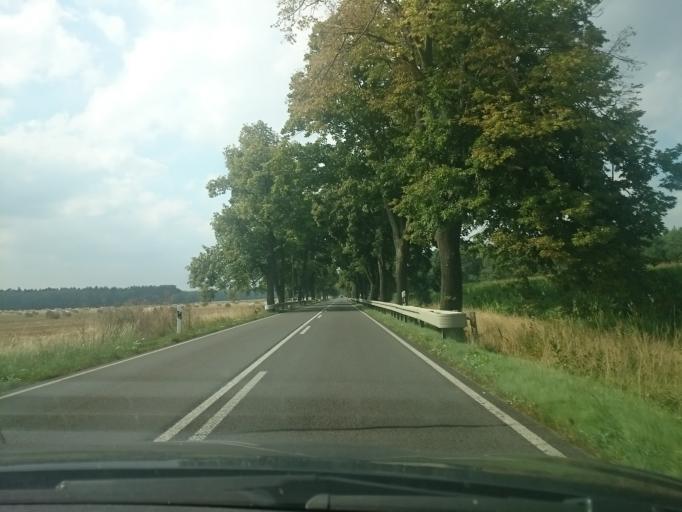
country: DE
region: Mecklenburg-Vorpommern
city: Ducherow
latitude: 53.7234
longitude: 13.8192
